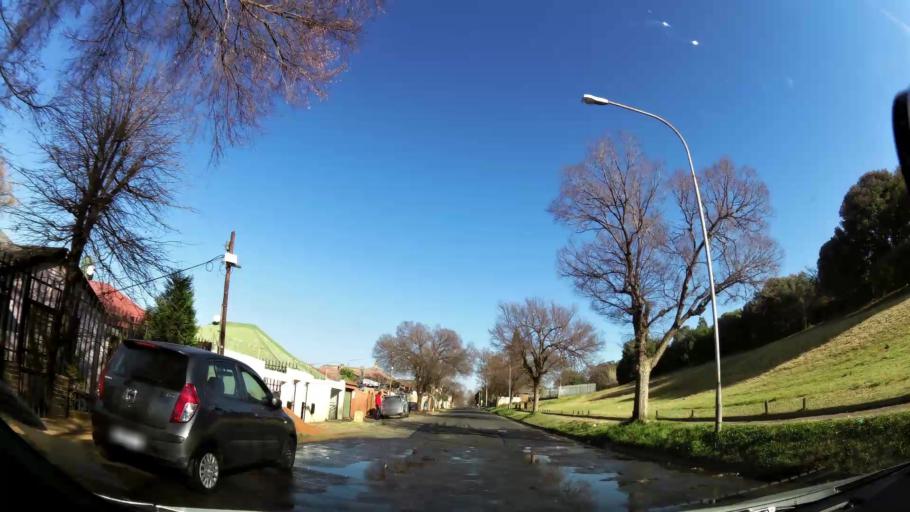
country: ZA
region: Gauteng
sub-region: City of Johannesburg Metropolitan Municipality
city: Johannesburg
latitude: -26.2030
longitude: 28.0937
